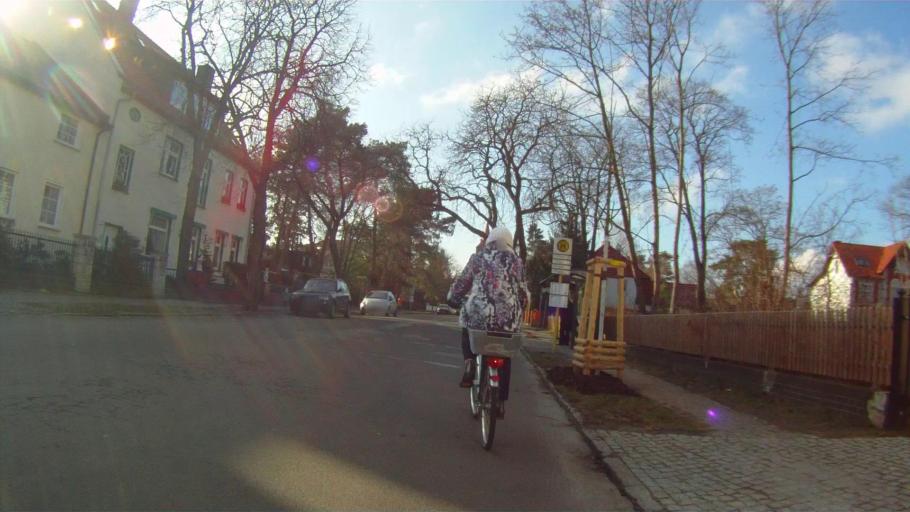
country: DE
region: Berlin
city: Rahnsdorf
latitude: 52.4367
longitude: 13.7175
